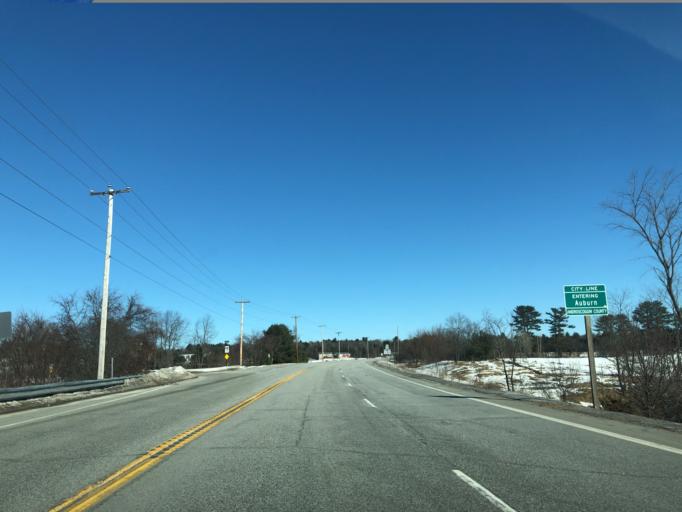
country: US
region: Maine
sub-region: Cumberland County
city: New Gloucester
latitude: 44.0158
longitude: -70.2860
